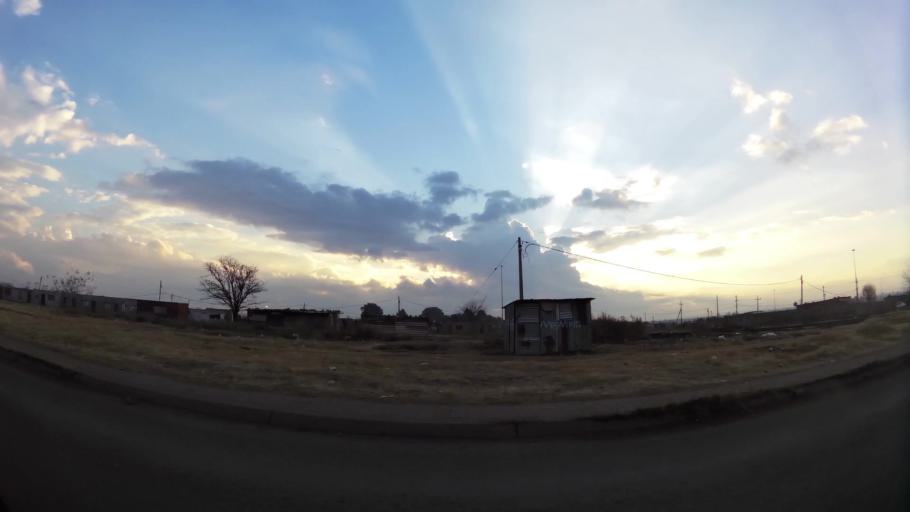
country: ZA
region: Gauteng
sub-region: City of Johannesburg Metropolitan Municipality
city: Orange Farm
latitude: -26.5516
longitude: 27.8404
